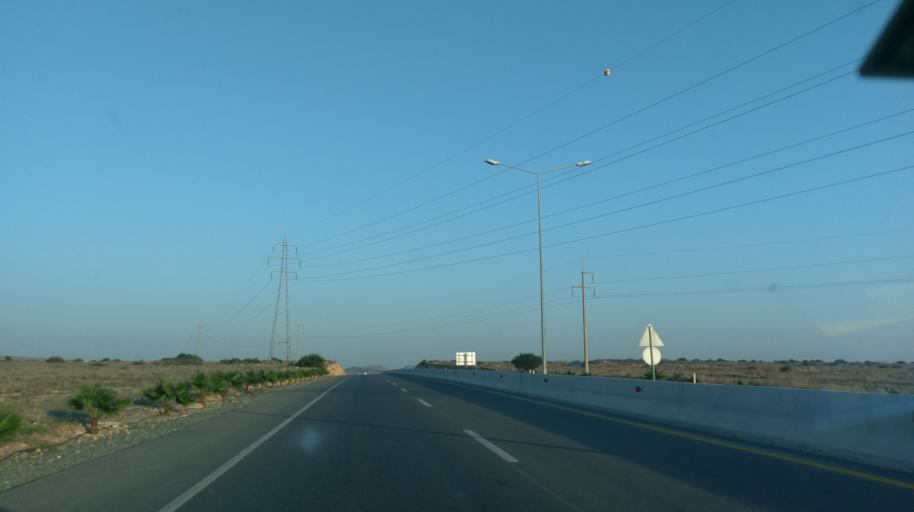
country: CY
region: Lefkosia
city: Astromeritis
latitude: 35.1960
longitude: 33.0675
